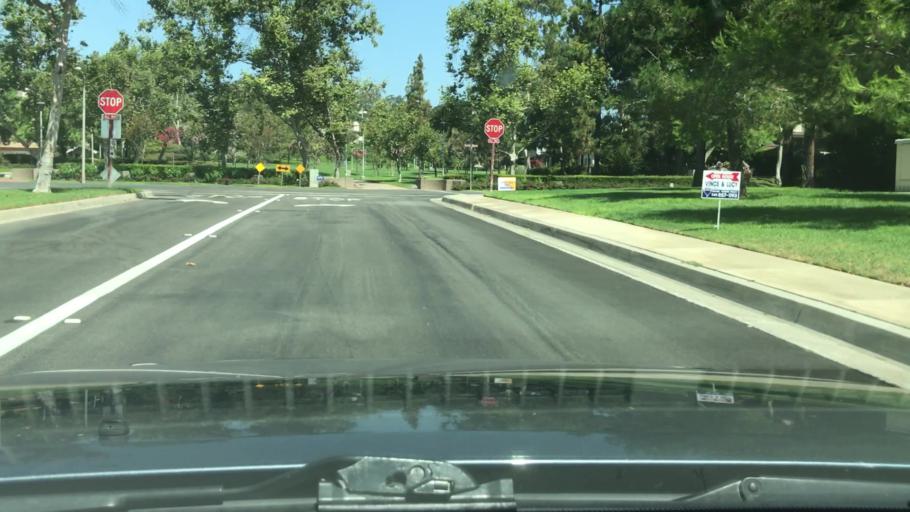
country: US
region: California
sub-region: Orange County
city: Irvine
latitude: 33.6349
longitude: -117.8036
